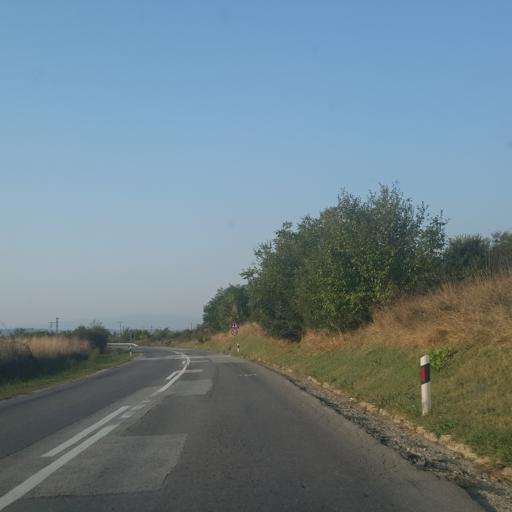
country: RS
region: Central Serbia
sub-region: Zajecarski Okrug
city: Zajecar
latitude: 43.9299
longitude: 22.2997
